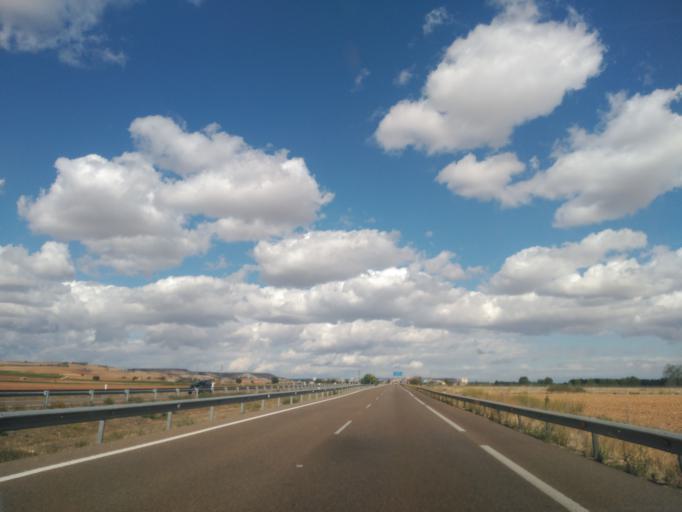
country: ES
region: Castille and Leon
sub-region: Provincia de Palencia
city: Torquemada
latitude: 42.0216
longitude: -4.3357
